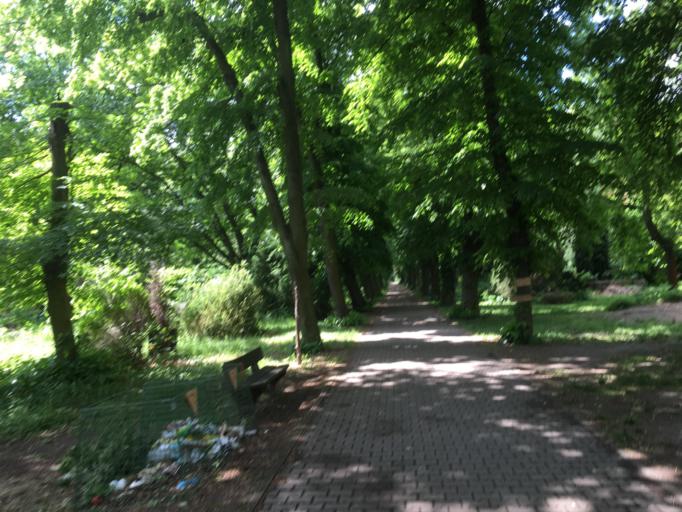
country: DE
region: Berlin
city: Britz
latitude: 52.4690
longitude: 13.4271
